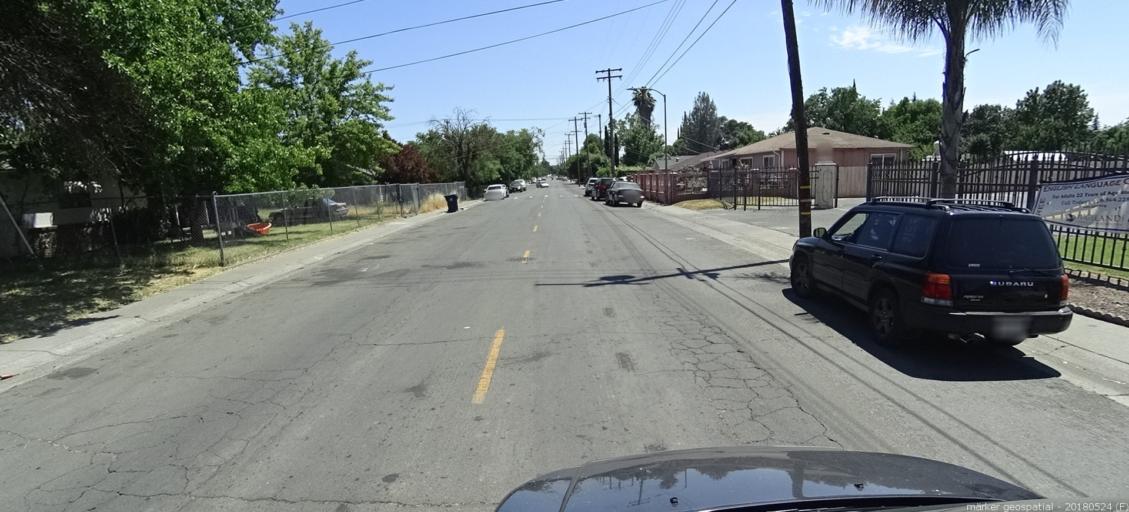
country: US
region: California
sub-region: Sacramento County
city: Sacramento
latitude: 38.6182
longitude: -121.4594
